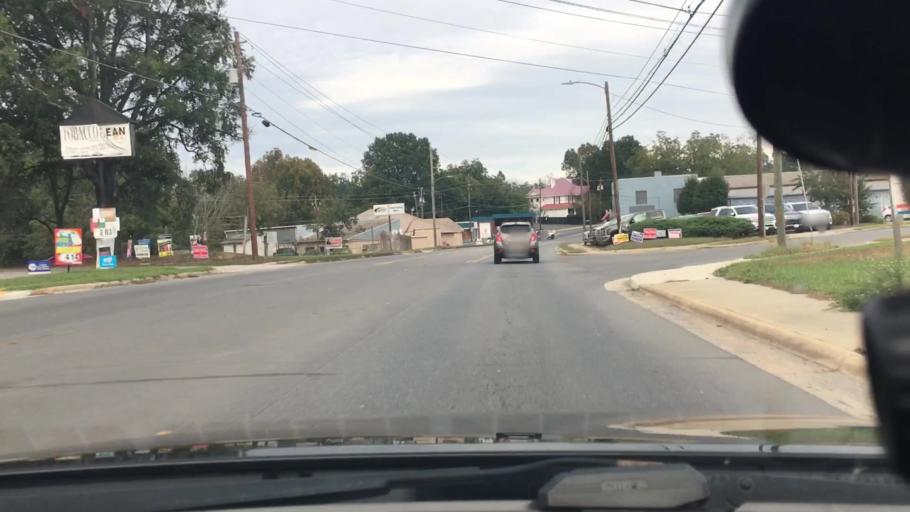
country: US
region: North Carolina
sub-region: Montgomery County
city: Troy
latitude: 35.3577
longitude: -79.8976
